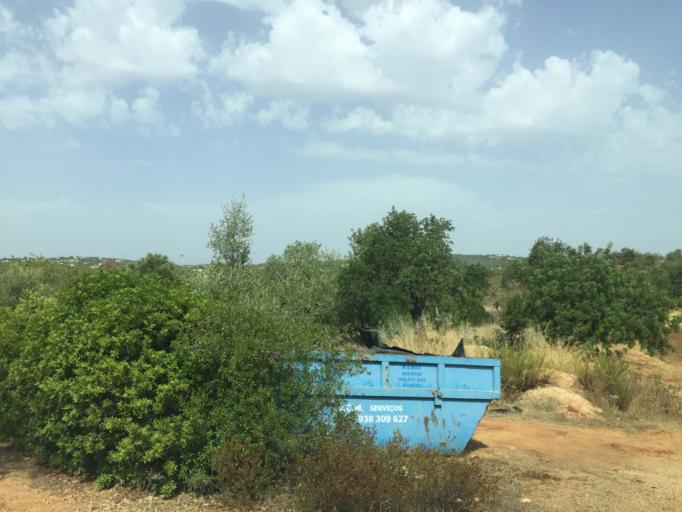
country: PT
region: Faro
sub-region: Loule
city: Boliqueime
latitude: 37.1318
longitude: -8.1341
